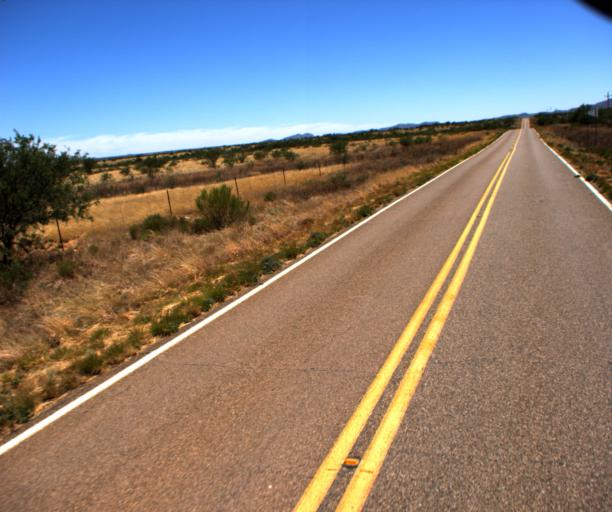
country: US
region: Arizona
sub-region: Pima County
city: Arivaca Junction
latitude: 31.6184
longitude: -111.5148
